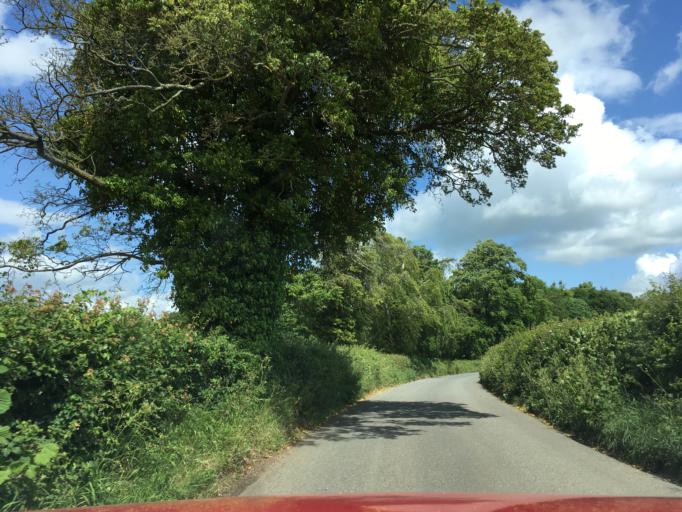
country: GB
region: England
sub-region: Gloucestershire
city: Stroud
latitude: 51.7609
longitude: -2.2129
